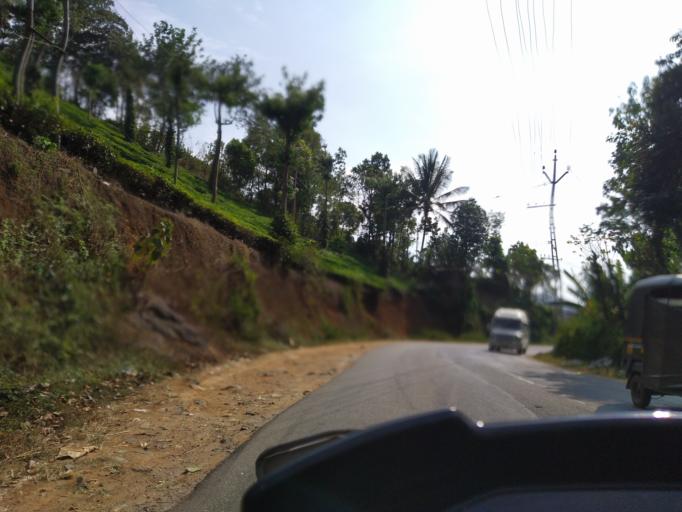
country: IN
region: Tamil Nadu
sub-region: Theni
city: Gudalur
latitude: 9.5913
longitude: 77.1235
